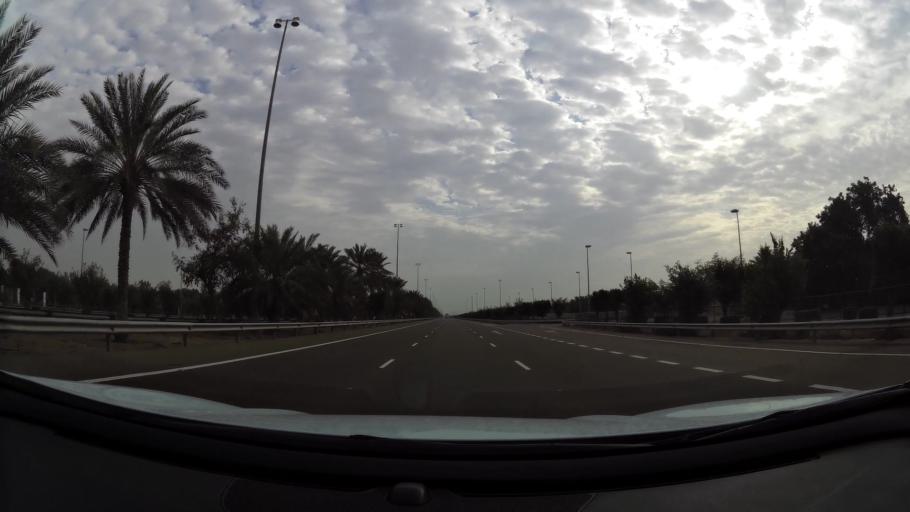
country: AE
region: Abu Dhabi
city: Al Ain
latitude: 24.1773
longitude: 55.3109
